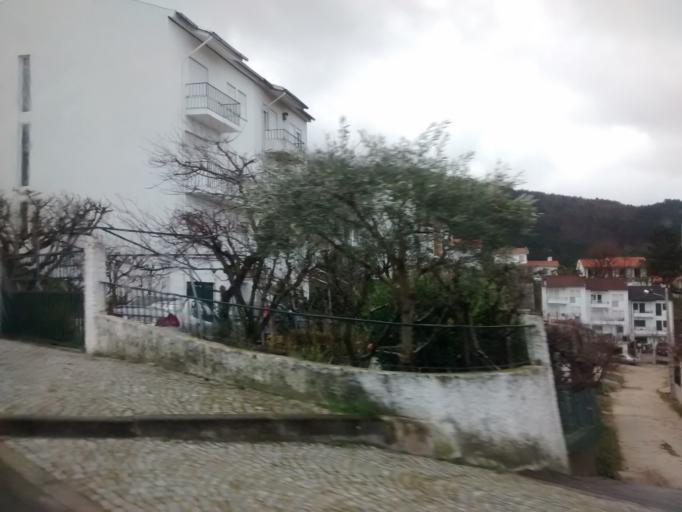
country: PT
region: Guarda
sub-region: Seia
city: Seia
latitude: 40.4130
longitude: -7.7022
